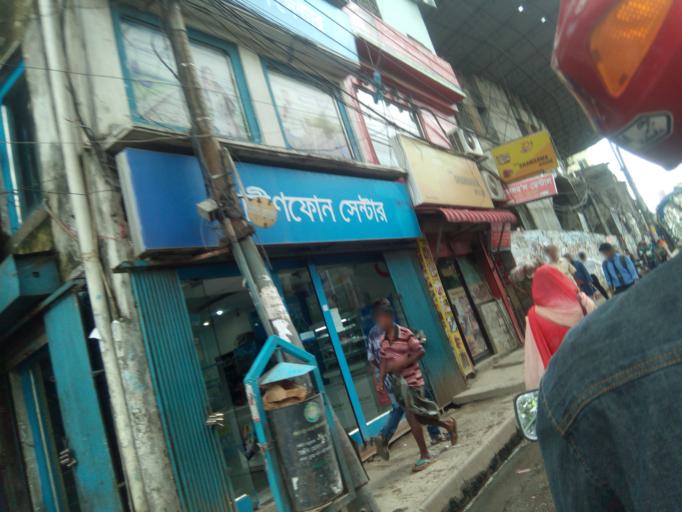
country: BD
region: Dhaka
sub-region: Dhaka
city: Dhaka
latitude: 23.7130
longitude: 90.4115
